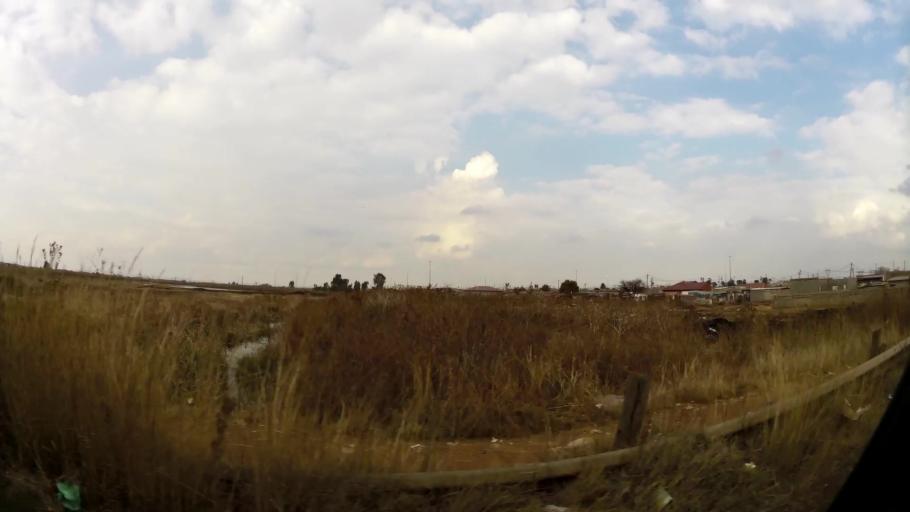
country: ZA
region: Gauteng
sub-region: Sedibeng District Municipality
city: Vanderbijlpark
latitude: -26.6722
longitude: 27.8602
